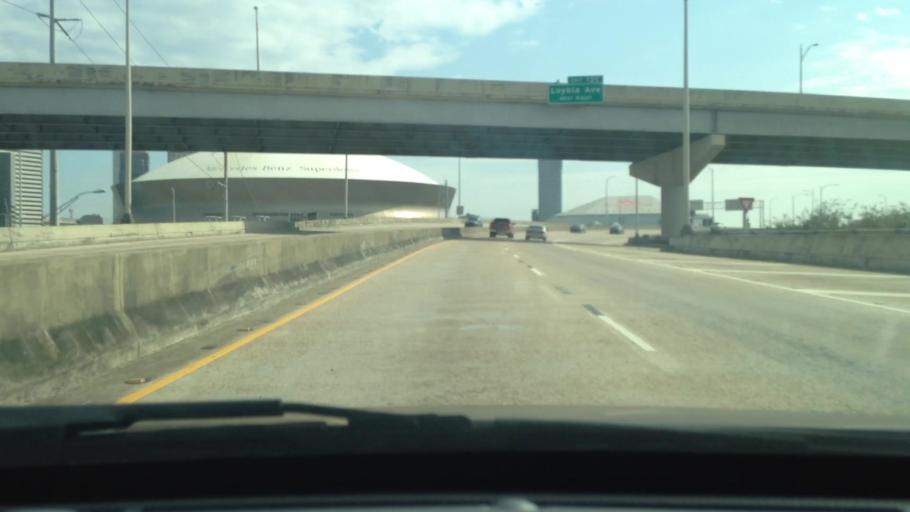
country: US
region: Louisiana
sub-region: Orleans Parish
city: New Orleans
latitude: 29.9530
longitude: -90.0875
